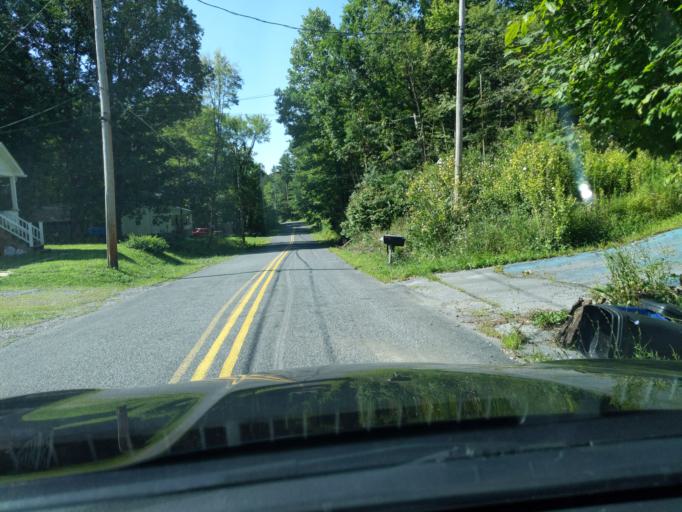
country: US
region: Pennsylvania
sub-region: Blair County
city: Altoona
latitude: 40.5462
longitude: -78.4046
